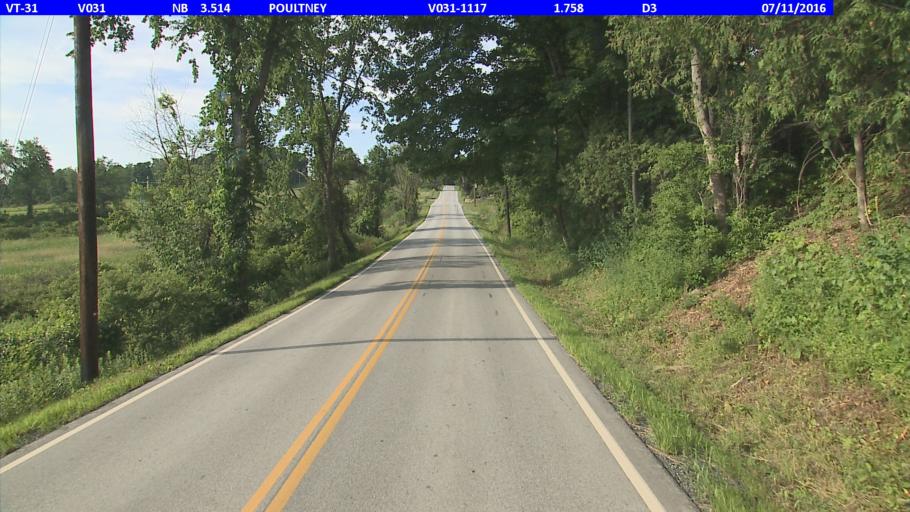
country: US
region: Vermont
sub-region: Rutland County
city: Poultney
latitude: 43.4871
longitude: -73.2398
